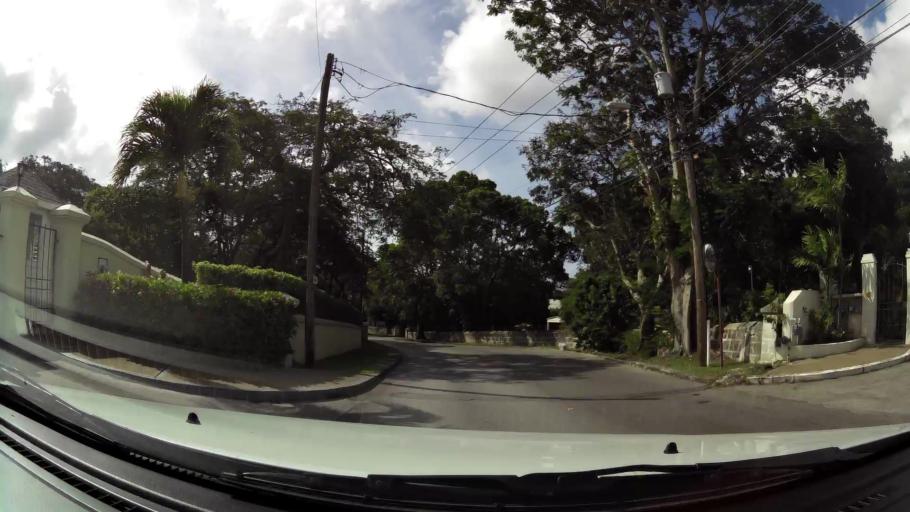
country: BB
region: Saint Michael
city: Bridgetown
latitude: 13.1003
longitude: -59.5956
